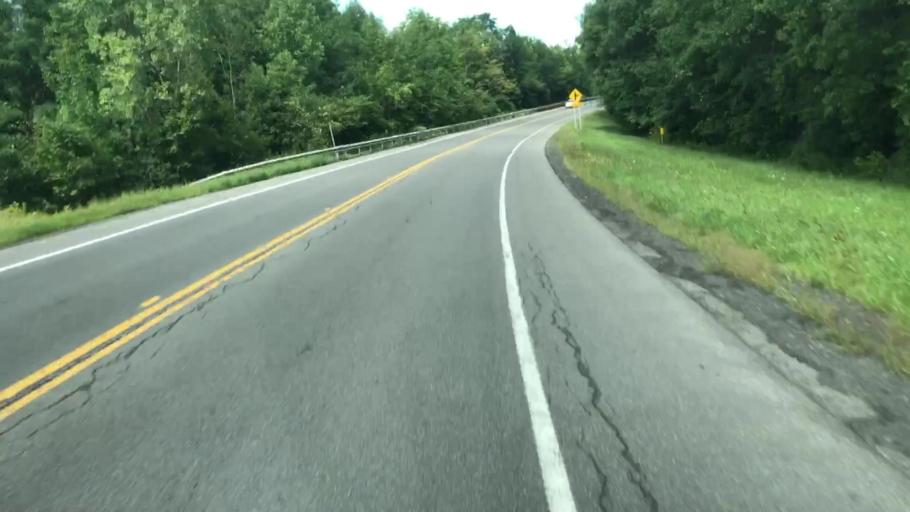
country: US
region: New York
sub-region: Onondaga County
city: Marcellus
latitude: 42.9712
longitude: -76.3371
